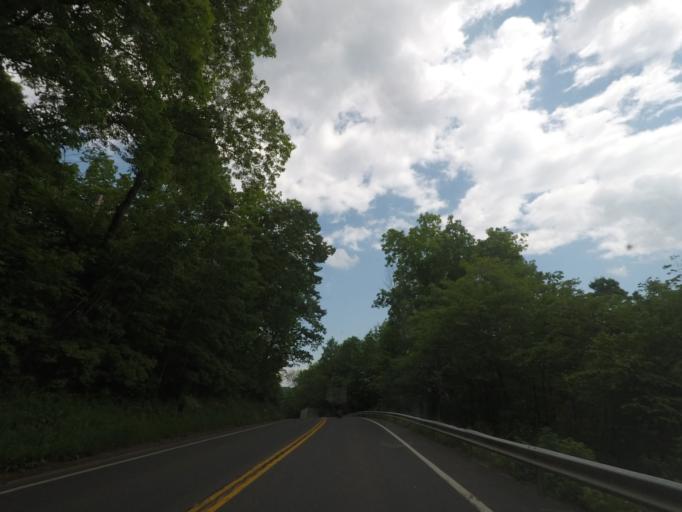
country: US
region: New York
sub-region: Dutchess County
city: Pine Plains
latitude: 42.0529
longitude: -73.6434
